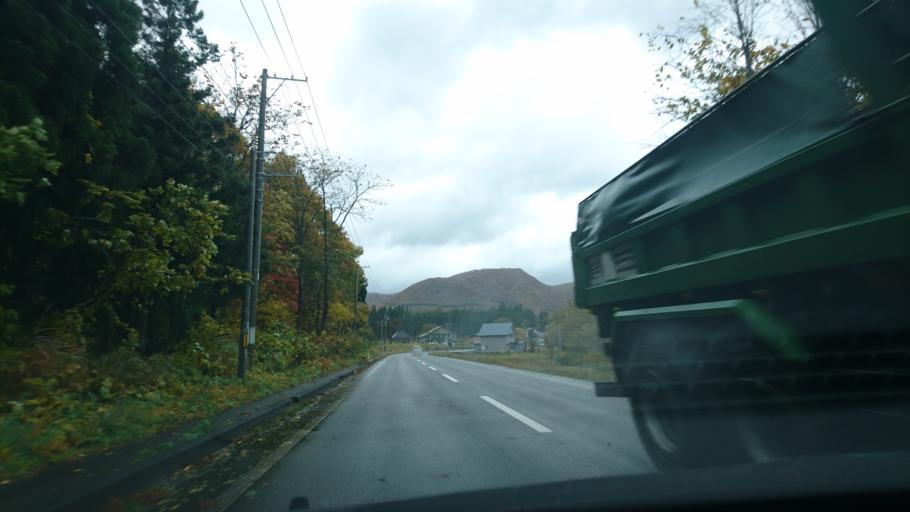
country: JP
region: Akita
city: Kakunodatemachi
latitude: 39.4708
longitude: 140.7817
